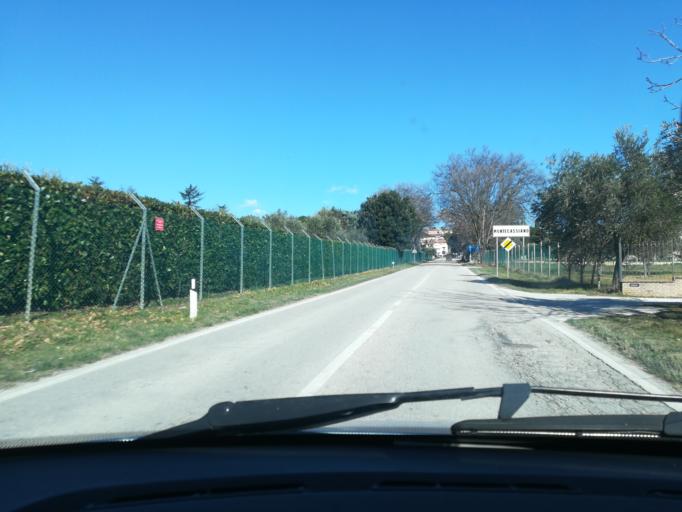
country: IT
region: The Marches
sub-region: Provincia di Macerata
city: Montecassiano
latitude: 43.3587
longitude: 13.4407
